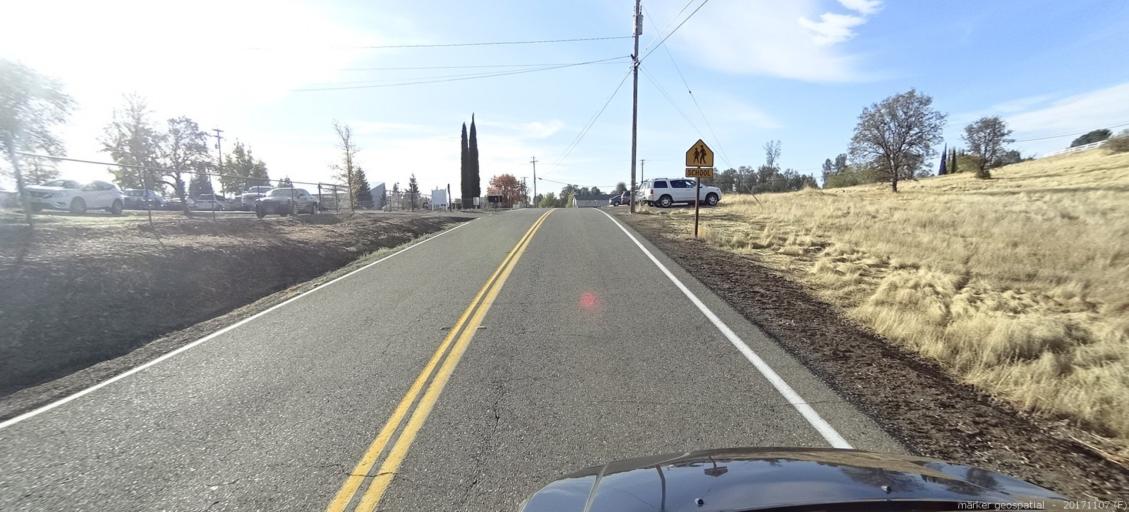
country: US
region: California
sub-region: Shasta County
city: Shasta
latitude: 40.5426
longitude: -122.4739
